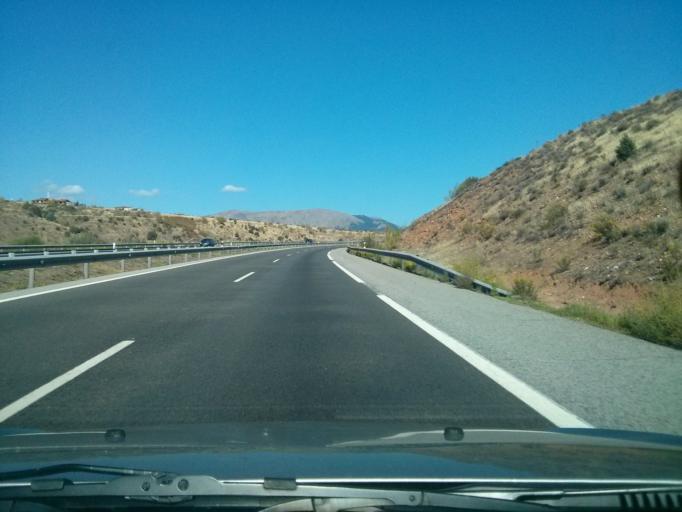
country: ES
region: Madrid
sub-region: Provincia de Madrid
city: Venturada
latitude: 40.8046
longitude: -3.6185
